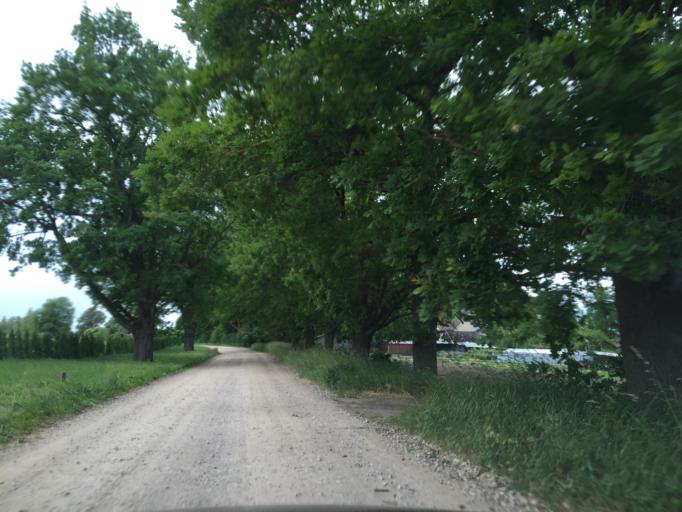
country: LV
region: Lecava
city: Iecava
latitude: 56.5848
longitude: 24.2013
